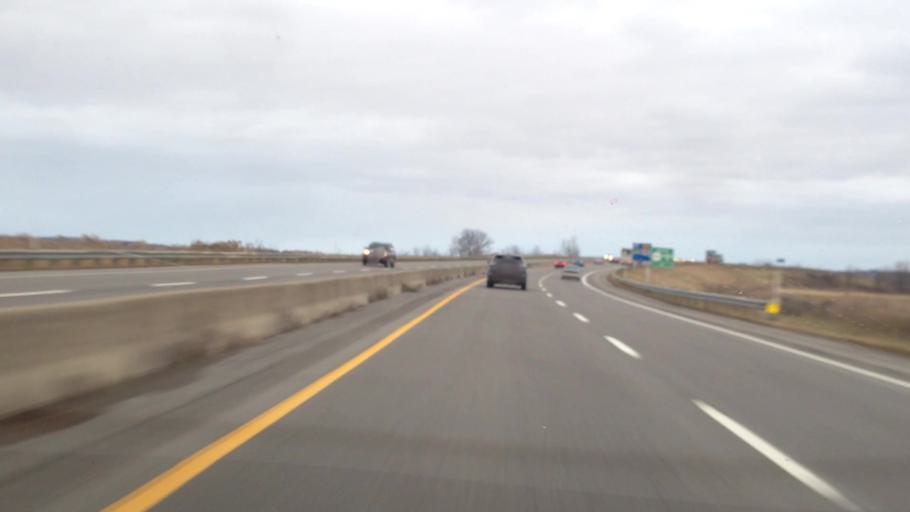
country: CA
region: Quebec
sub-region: Monteregie
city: Rigaud
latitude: 45.4846
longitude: -74.2932
